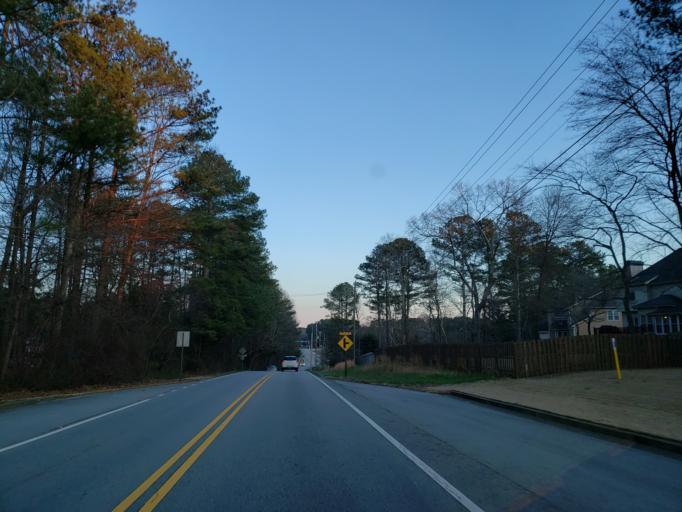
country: US
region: Georgia
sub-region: Cobb County
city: Acworth
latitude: 33.9924
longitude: -84.7144
